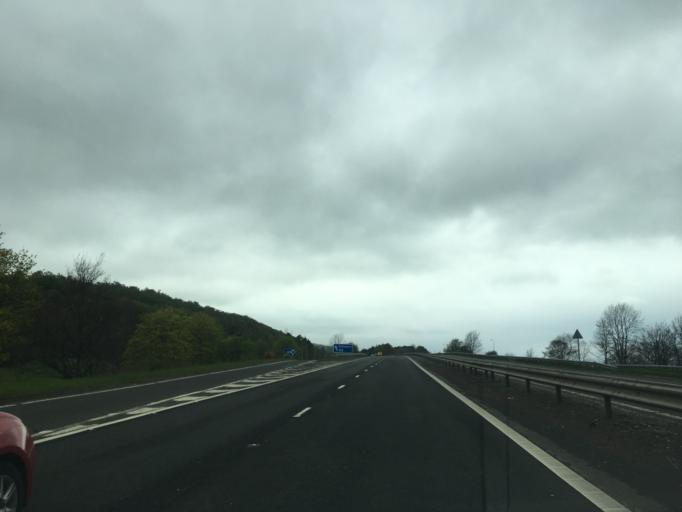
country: GB
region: Scotland
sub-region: West Dunbartonshire
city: Dumbarton
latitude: 55.9234
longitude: -4.5505
